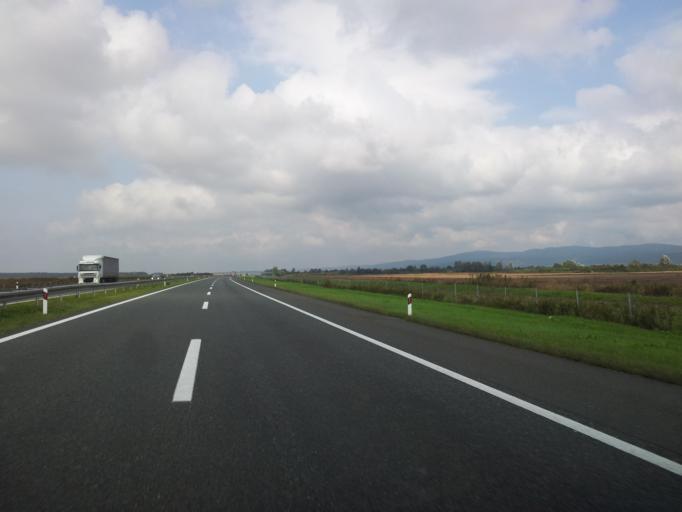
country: HR
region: Brodsko-Posavska
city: Okucani
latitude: 45.2706
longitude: 17.1385
